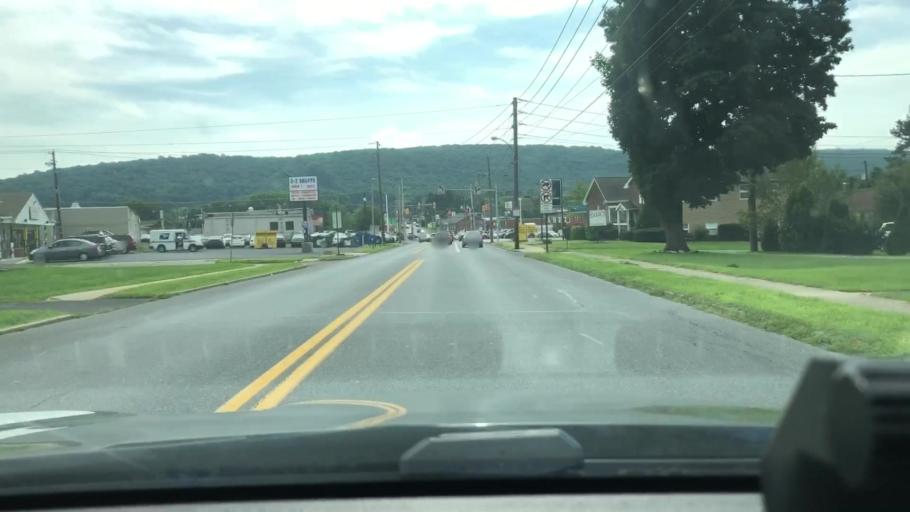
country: US
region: Pennsylvania
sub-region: Lehigh County
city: Emmaus
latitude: 40.5596
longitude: -75.4894
